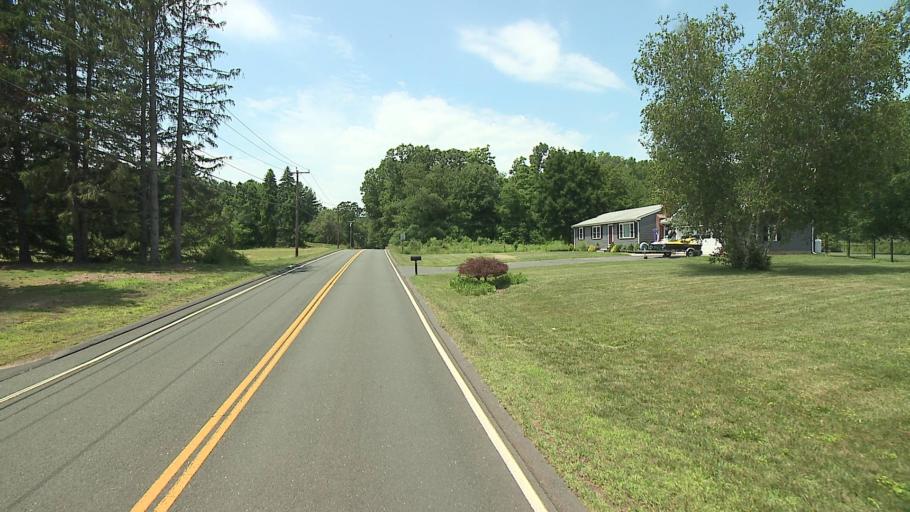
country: US
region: Connecticut
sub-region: Hartford County
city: Tariffville
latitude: 41.9173
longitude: -72.7410
